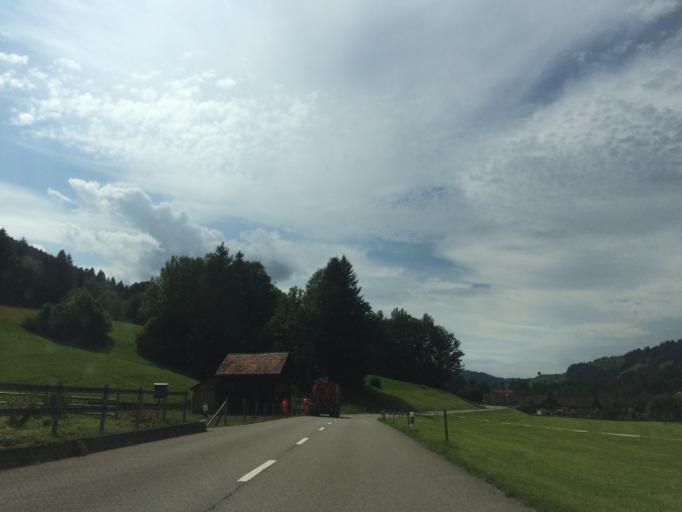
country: CH
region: Saint Gallen
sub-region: Wahlkreis Toggenburg
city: Krummenau
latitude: 47.2437
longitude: 9.2416
